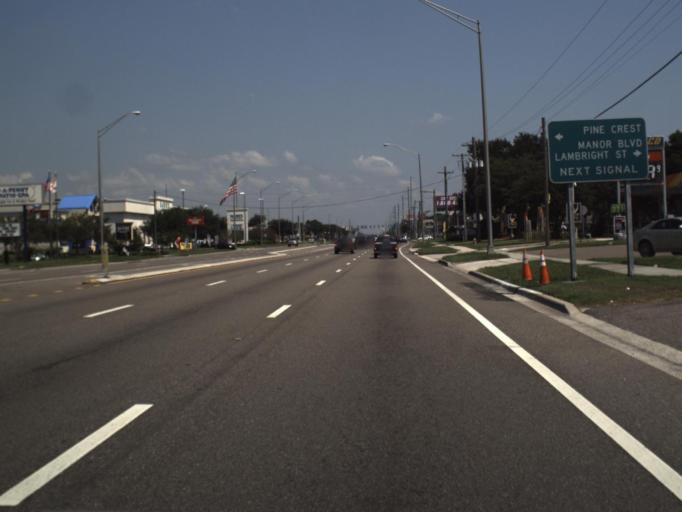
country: US
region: Florida
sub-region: Hillsborough County
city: Egypt Lake-Leto
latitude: 28.0032
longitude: -82.5051
